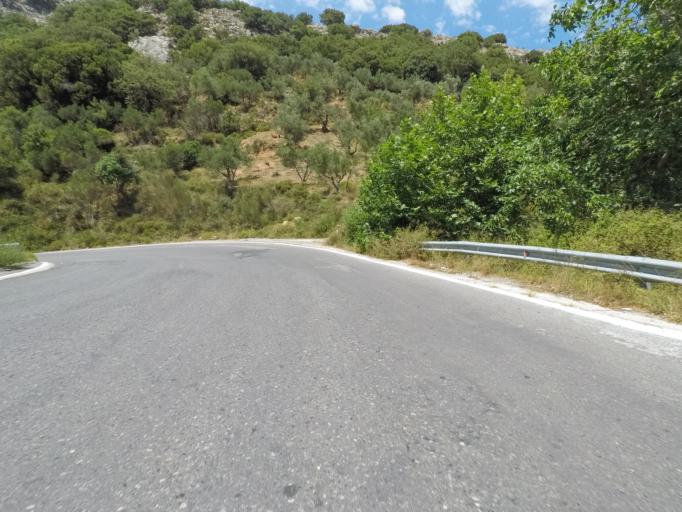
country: GR
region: Crete
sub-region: Nomos Irakleiou
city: Mokhos
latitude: 35.2303
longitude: 25.4635
